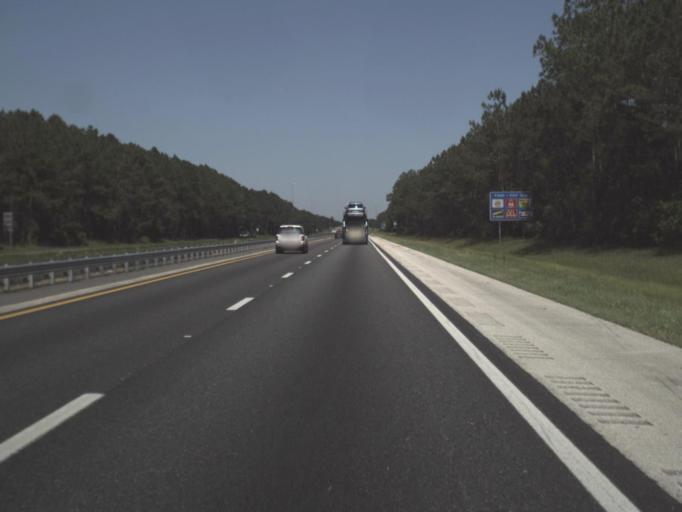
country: US
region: Florida
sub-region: Duval County
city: Baldwin
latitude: 30.2878
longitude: -81.9970
